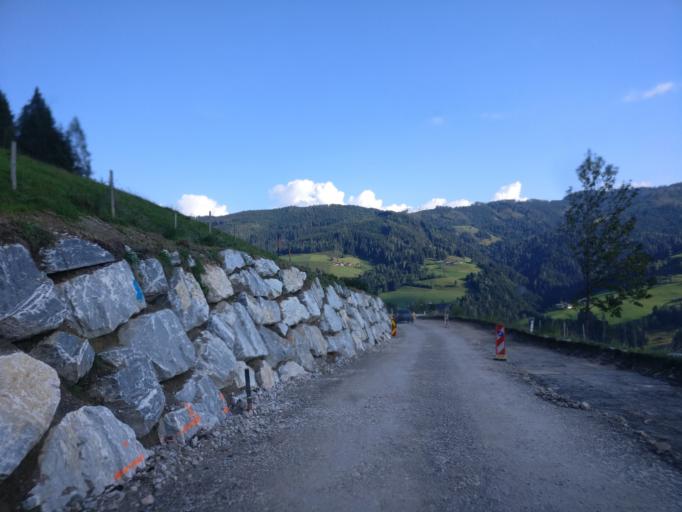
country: AT
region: Salzburg
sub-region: Politischer Bezirk Sankt Johann im Pongau
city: Muhlbach am Hochkonig
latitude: 47.3837
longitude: 13.1227
